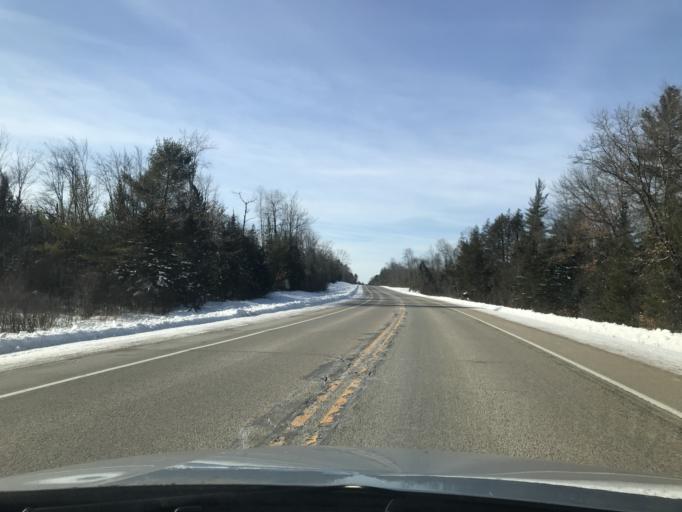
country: US
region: Wisconsin
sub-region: Oconto County
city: Gillett
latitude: 45.1282
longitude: -88.4076
